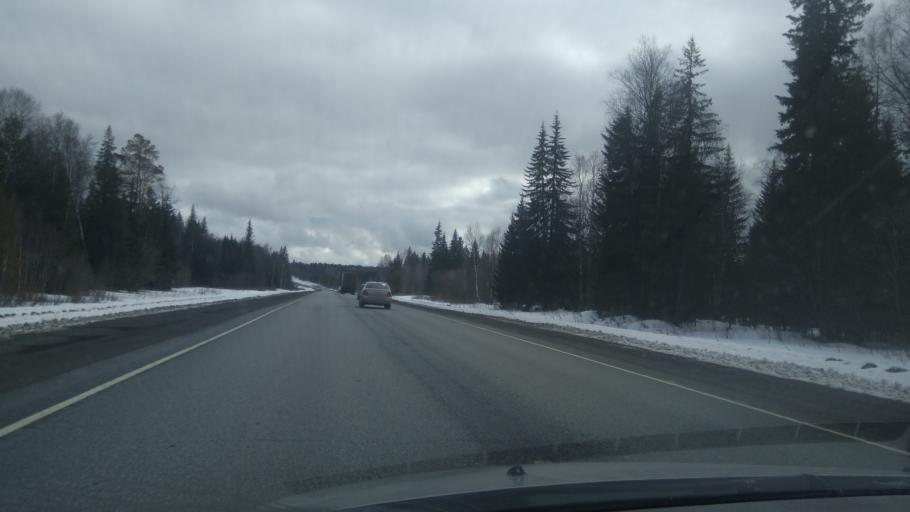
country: RU
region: Sverdlovsk
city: Atig
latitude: 56.8089
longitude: 59.3667
